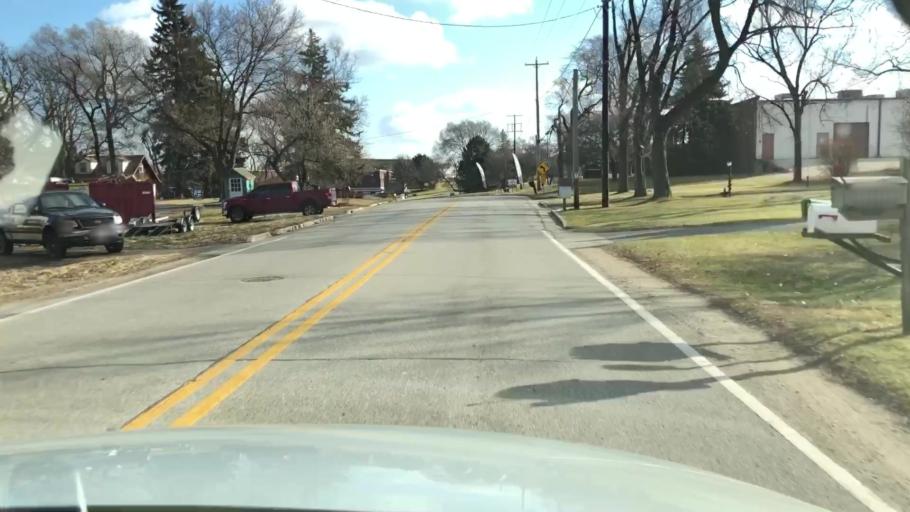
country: US
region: Wisconsin
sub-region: Waukesha County
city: Waukesha
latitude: 43.0389
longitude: -88.1725
